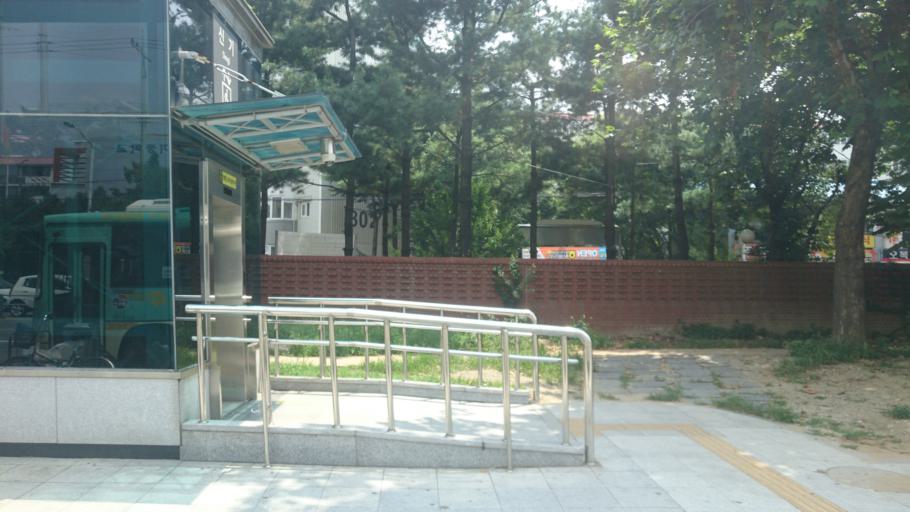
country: KR
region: Gyeongsangbuk-do
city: Gyeongsan-si
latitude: 35.8665
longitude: 128.7023
